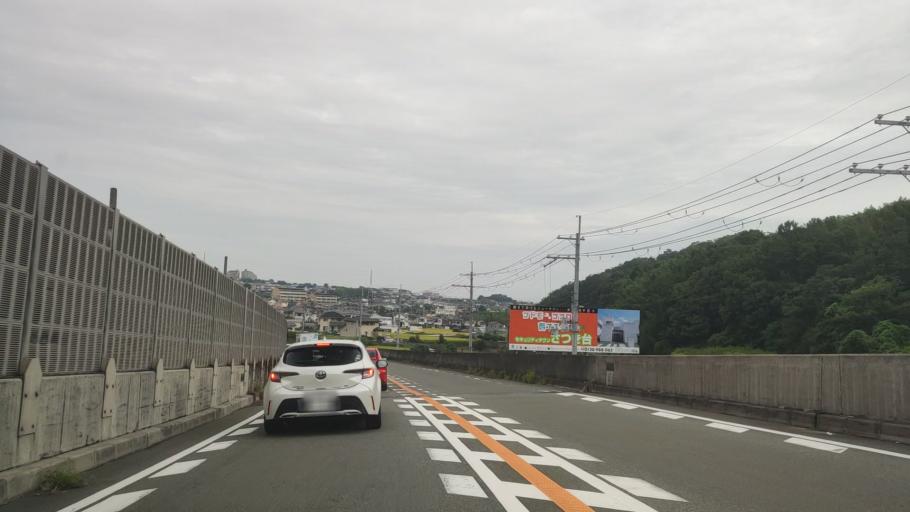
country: JP
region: Osaka
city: Tondabayashicho
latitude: 34.4401
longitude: 135.5589
